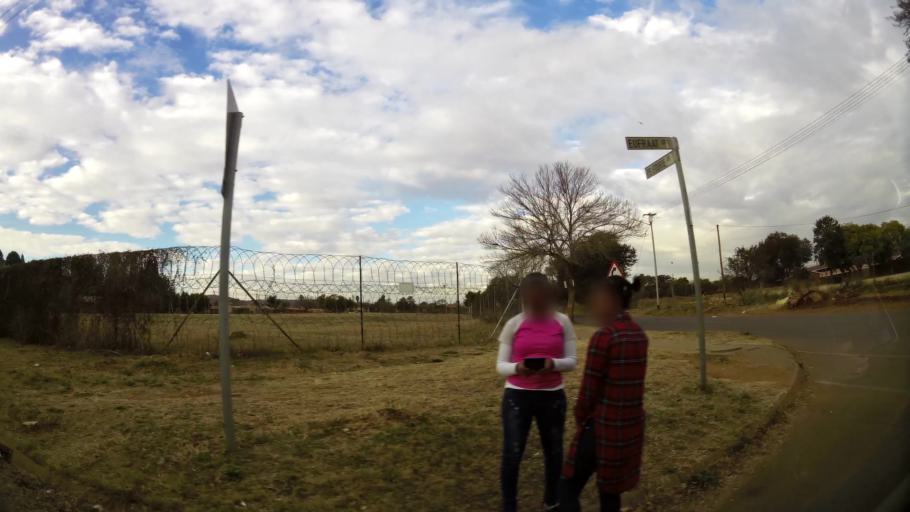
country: ZA
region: Gauteng
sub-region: City of Tshwane Metropolitan Municipality
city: Pretoria
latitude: -25.7067
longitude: 28.3136
